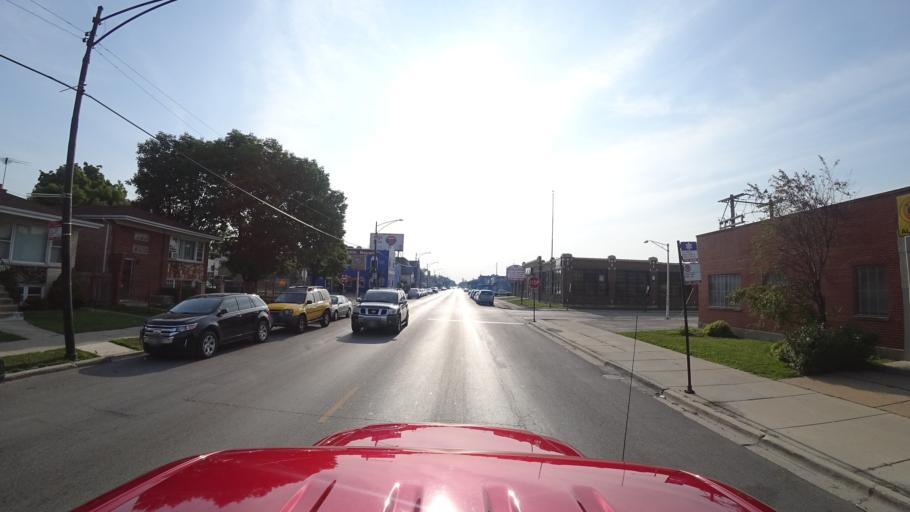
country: US
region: Illinois
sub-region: Cook County
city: Cicero
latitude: 41.8081
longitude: -87.7008
